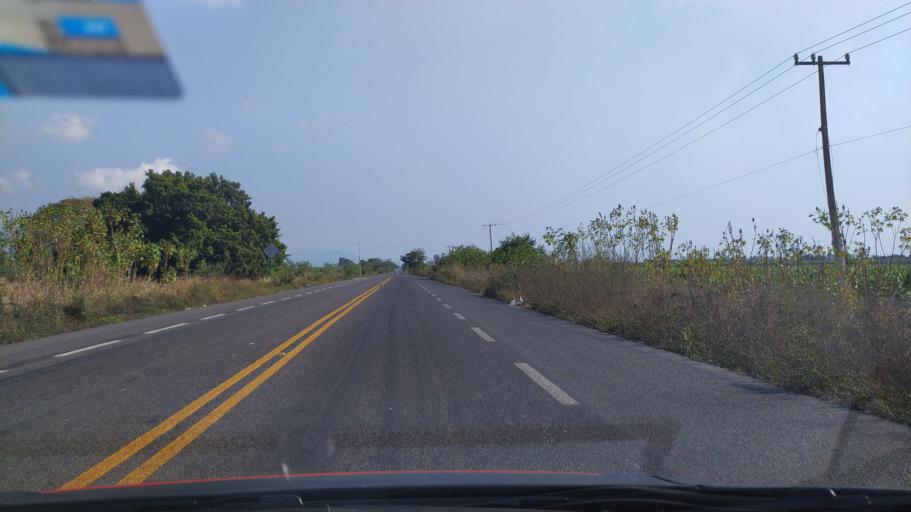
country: MX
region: Colima
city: Tecoman
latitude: 18.8162
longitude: -103.8068
